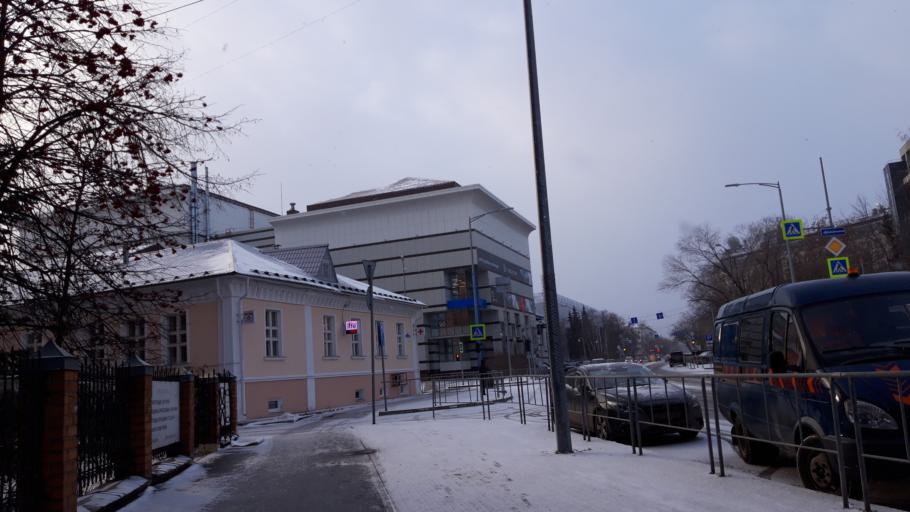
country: RU
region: Tjumen
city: Tyumen
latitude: 57.1550
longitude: 65.5509
